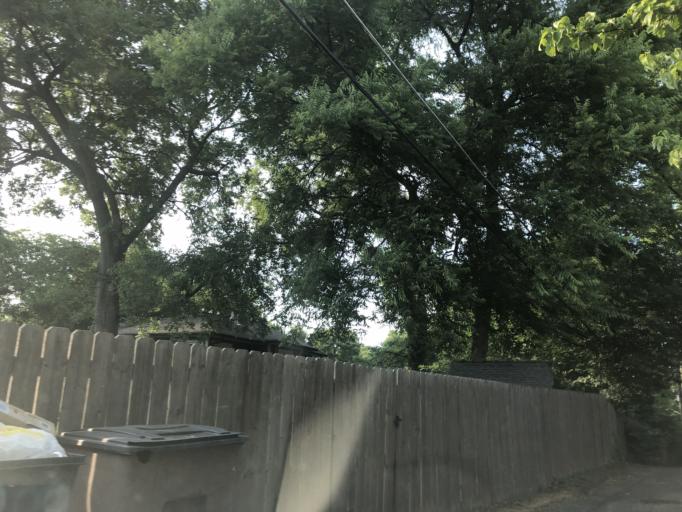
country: US
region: Tennessee
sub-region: Davidson County
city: Oak Hill
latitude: 36.1187
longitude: -86.7954
